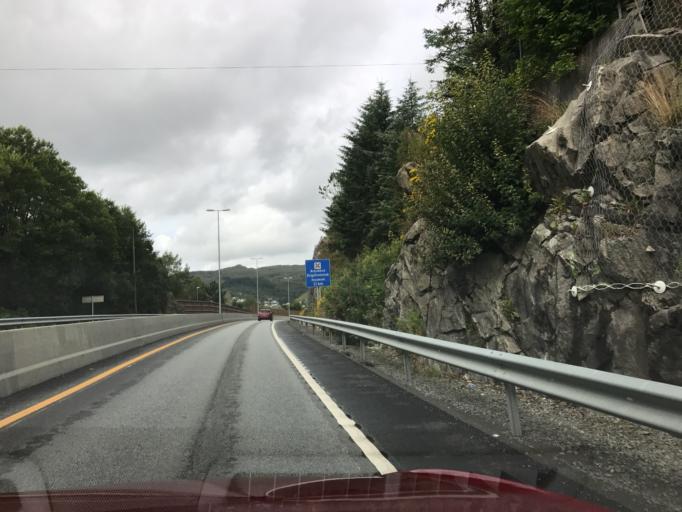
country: NO
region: Rogaland
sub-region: Karmoy
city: Eike
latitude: 59.4188
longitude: 5.3988
